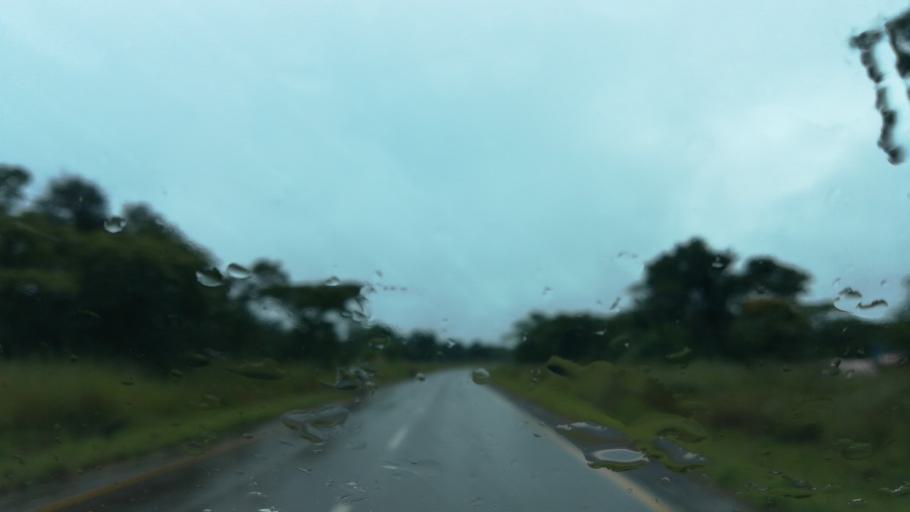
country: ZM
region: Luapula
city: Mwense
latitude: -10.8836
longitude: 28.2151
